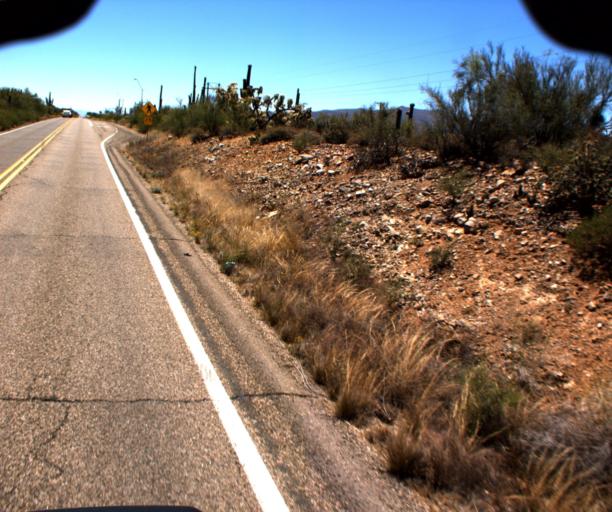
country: US
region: Arizona
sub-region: Pinal County
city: Kearny
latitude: 33.0673
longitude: -110.9132
